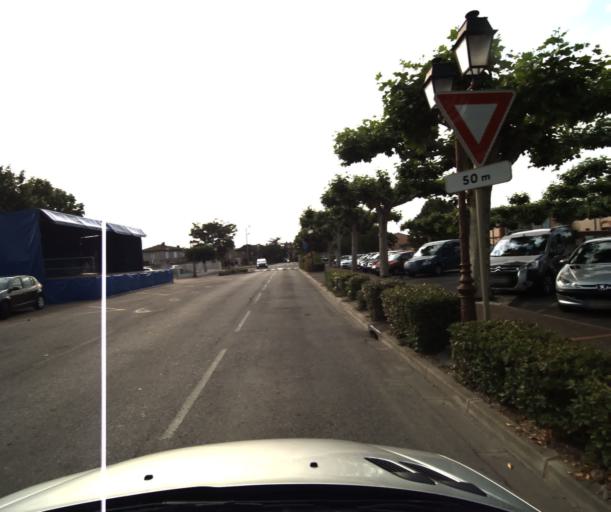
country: FR
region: Midi-Pyrenees
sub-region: Departement de la Haute-Garonne
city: Fonsorbes
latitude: 43.5332
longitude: 1.2306
